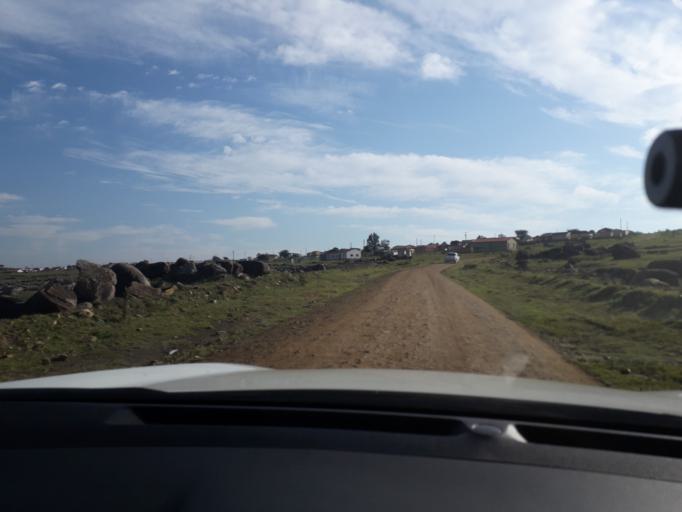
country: ZA
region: Eastern Cape
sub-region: Buffalo City Metropolitan Municipality
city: Bhisho
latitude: -32.9423
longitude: 27.2892
